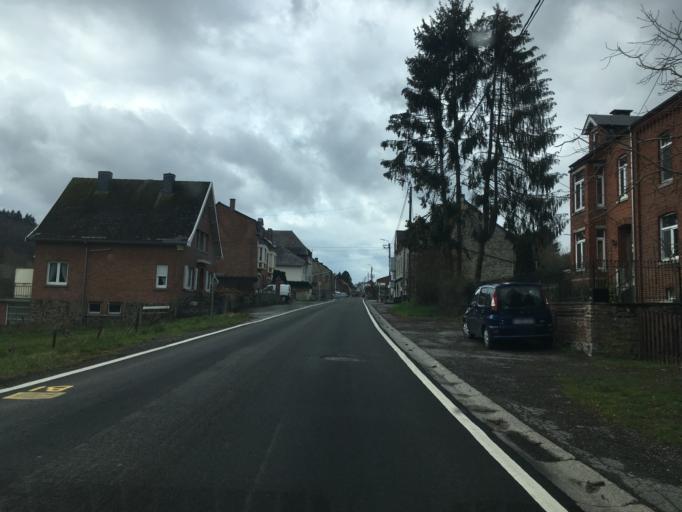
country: FR
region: Champagne-Ardenne
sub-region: Departement des Ardennes
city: Vireux-Molhain
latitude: 50.0919
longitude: 4.6834
